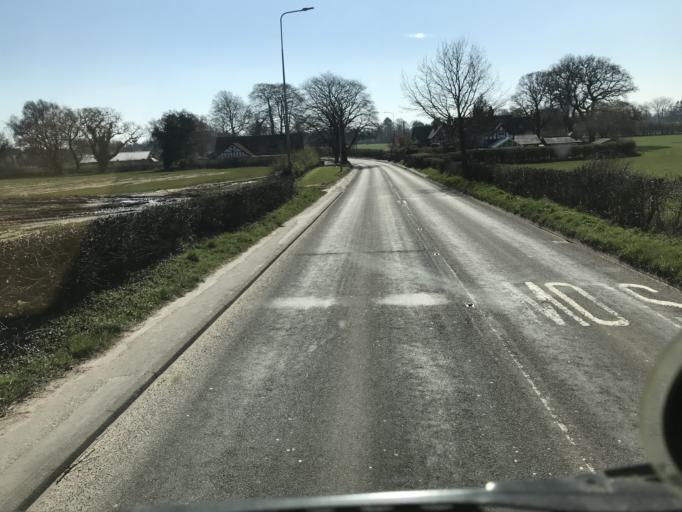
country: GB
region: England
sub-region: Cheshire East
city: Alderley Edge
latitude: 53.2694
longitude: -2.2796
